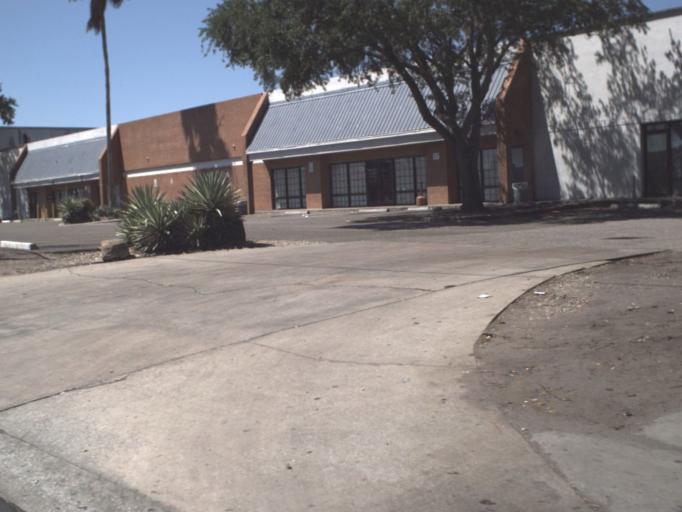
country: US
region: Florida
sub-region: Orange County
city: Azalea Park
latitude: 28.5609
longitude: -81.3110
